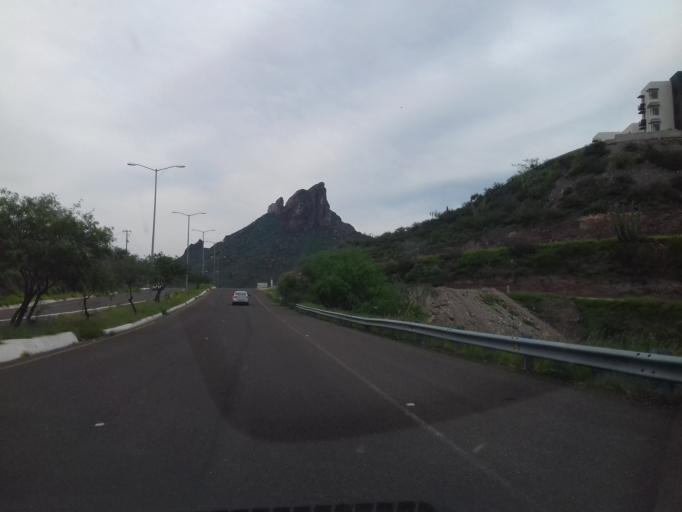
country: MX
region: Sonora
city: Heroica Guaymas
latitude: 27.9565
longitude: -111.0930
